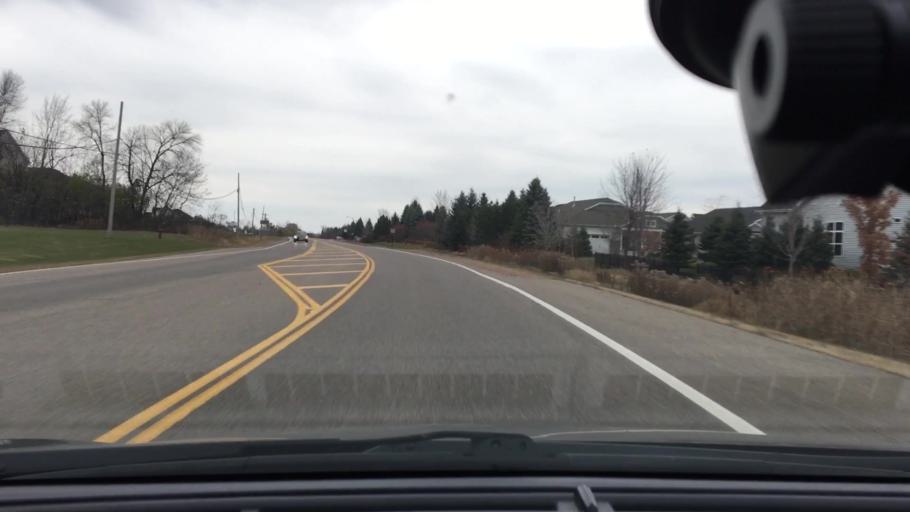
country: US
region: Minnesota
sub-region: Hennepin County
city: Corcoran
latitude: 45.0902
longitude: -93.5125
